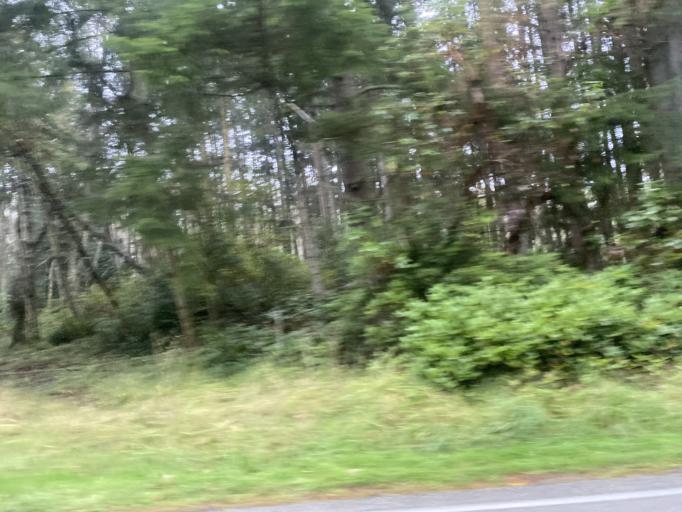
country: US
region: Washington
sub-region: Island County
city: Freeland
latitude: 48.0808
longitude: -122.4908
